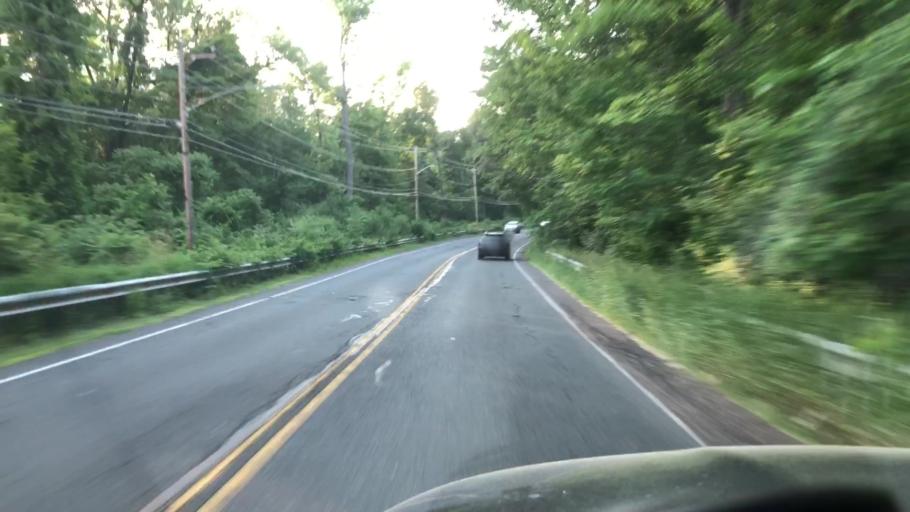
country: US
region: Massachusetts
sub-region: Hampshire County
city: Easthampton
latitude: 42.2318
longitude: -72.6488
